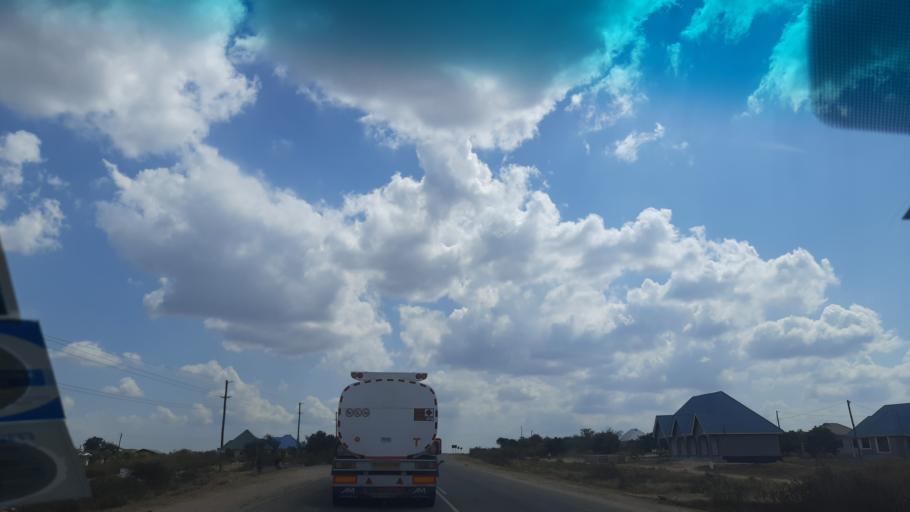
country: TZ
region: Dodoma
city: Dodoma
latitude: -6.0889
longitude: 35.6159
